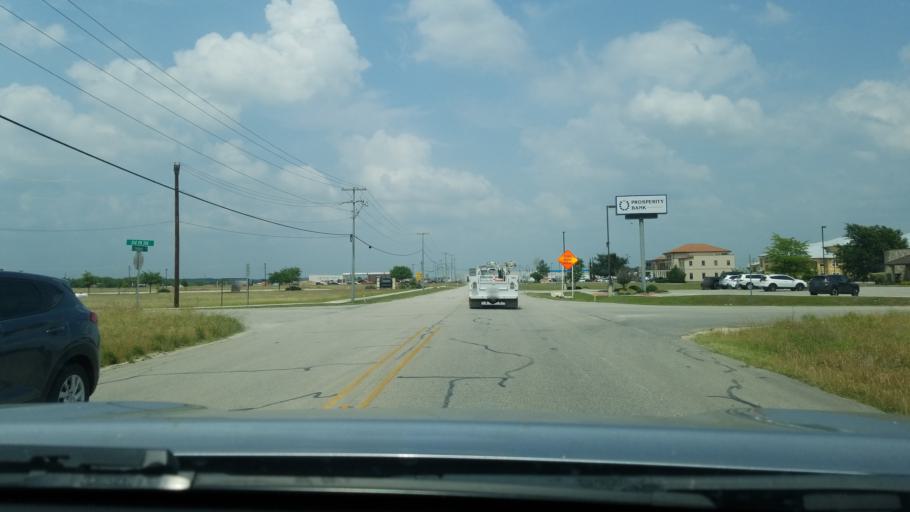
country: US
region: Texas
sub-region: Comal County
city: New Braunfels
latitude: 29.7388
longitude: -98.0962
